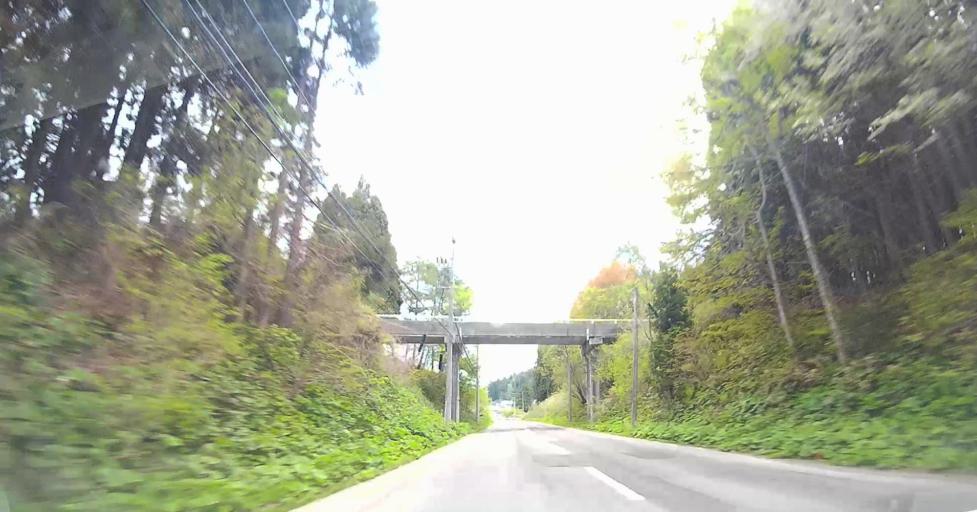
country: JP
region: Aomori
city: Shimokizukuri
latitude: 41.1803
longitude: 140.4617
